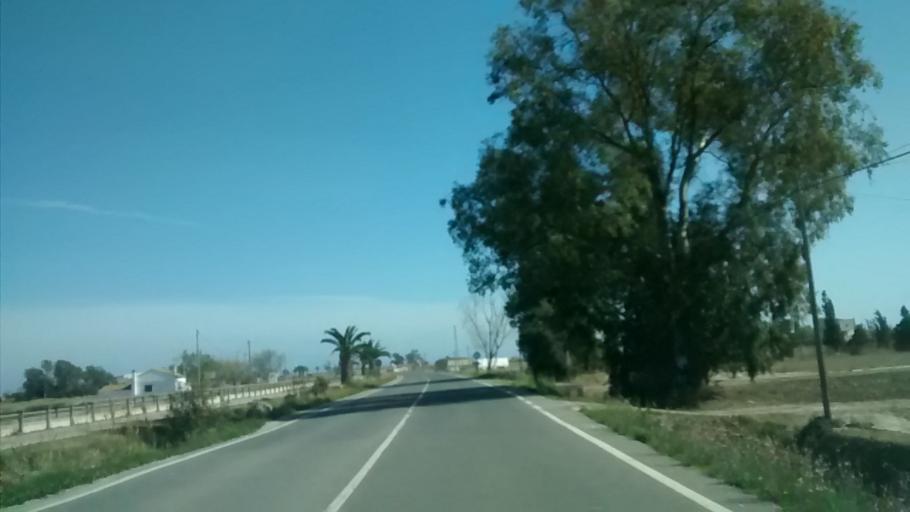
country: ES
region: Catalonia
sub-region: Provincia de Tarragona
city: Deltebre
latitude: 40.7107
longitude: 0.7578
